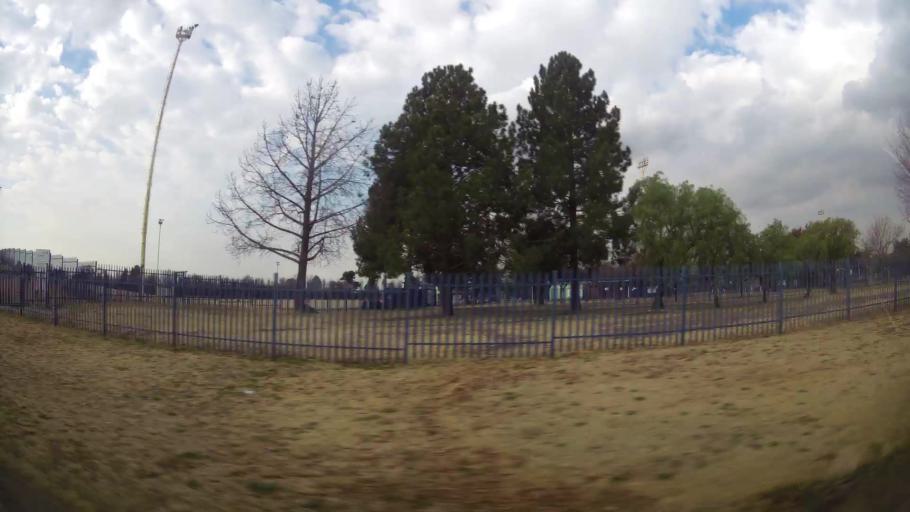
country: ZA
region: Orange Free State
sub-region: Fezile Dabi District Municipality
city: Sasolburg
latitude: -26.7940
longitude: 27.8242
